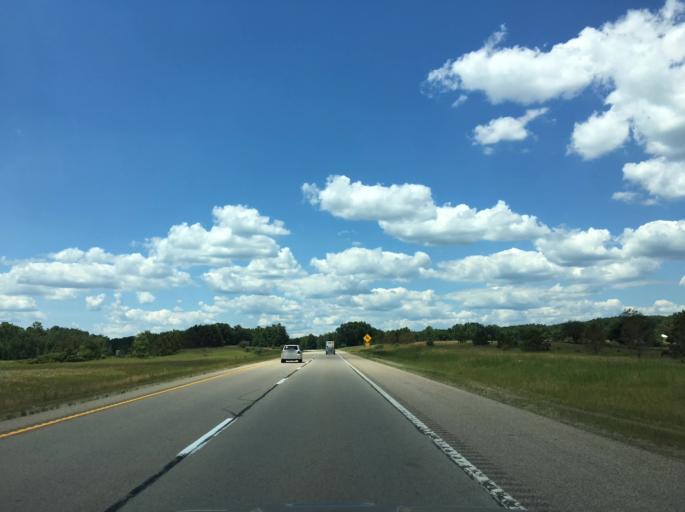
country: US
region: Michigan
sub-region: Clare County
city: Clare
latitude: 43.8831
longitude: -84.7962
